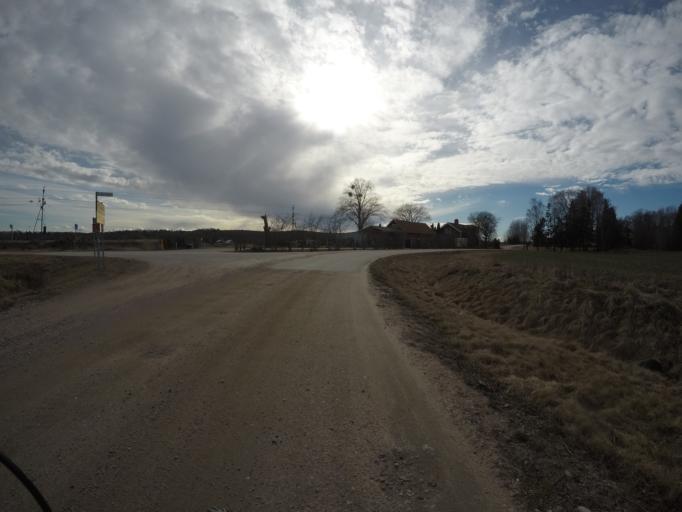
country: SE
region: Vaestmanland
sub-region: Kungsors Kommun
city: Kungsoer
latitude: 59.4164
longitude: 16.2001
